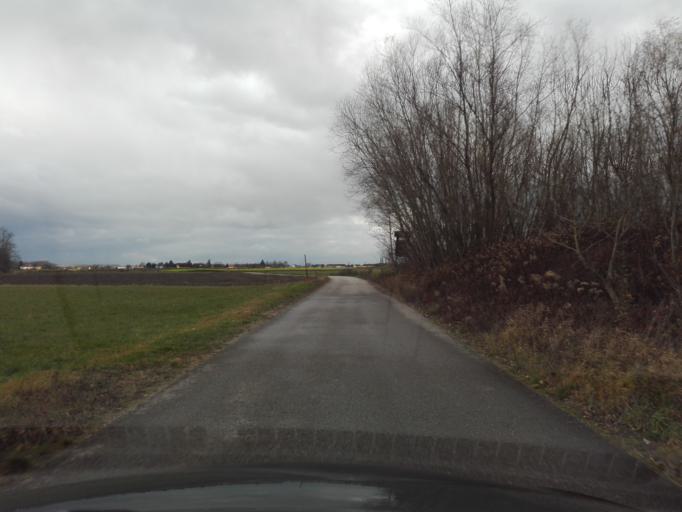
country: AT
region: Lower Austria
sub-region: Politischer Bezirk Amstetten
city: Strengberg
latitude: 48.1761
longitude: 14.6922
